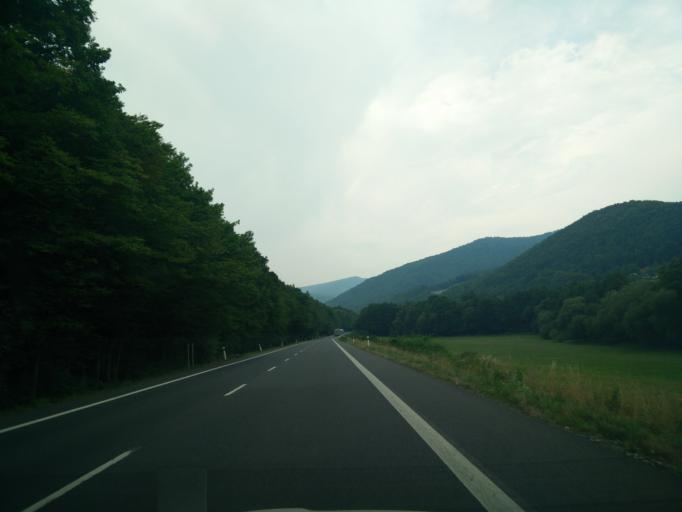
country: SK
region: Nitriansky
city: Handlova
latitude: 48.6461
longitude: 18.7647
